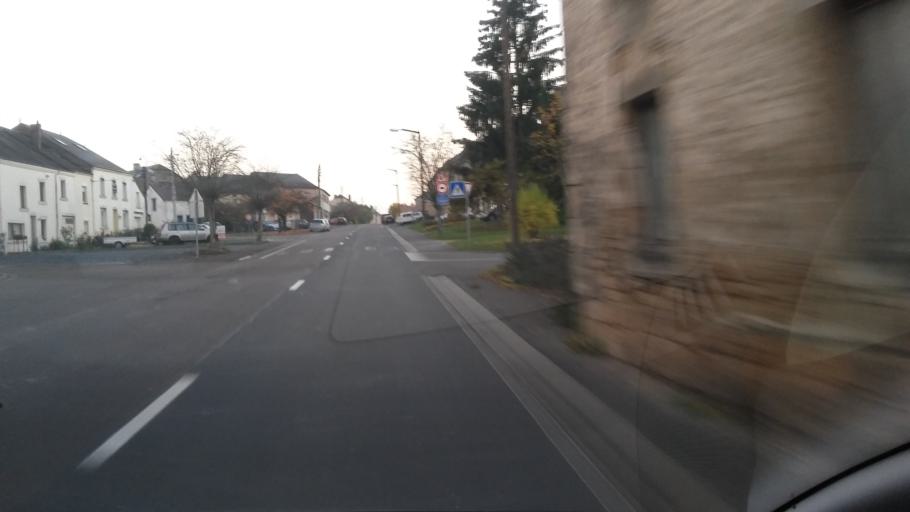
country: BE
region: Wallonia
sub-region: Province du Luxembourg
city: Etalle
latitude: 49.6721
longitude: 5.5996
